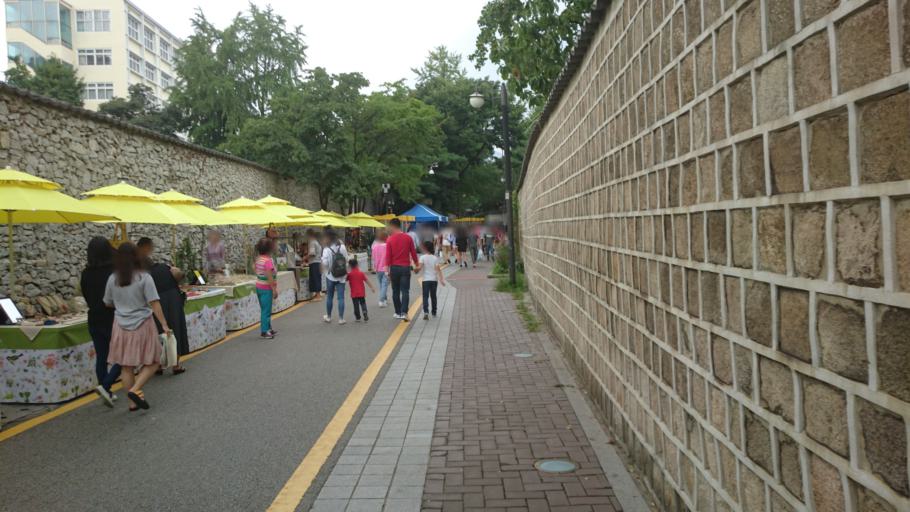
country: KR
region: Seoul
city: Seoul
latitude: 37.5769
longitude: 126.9825
